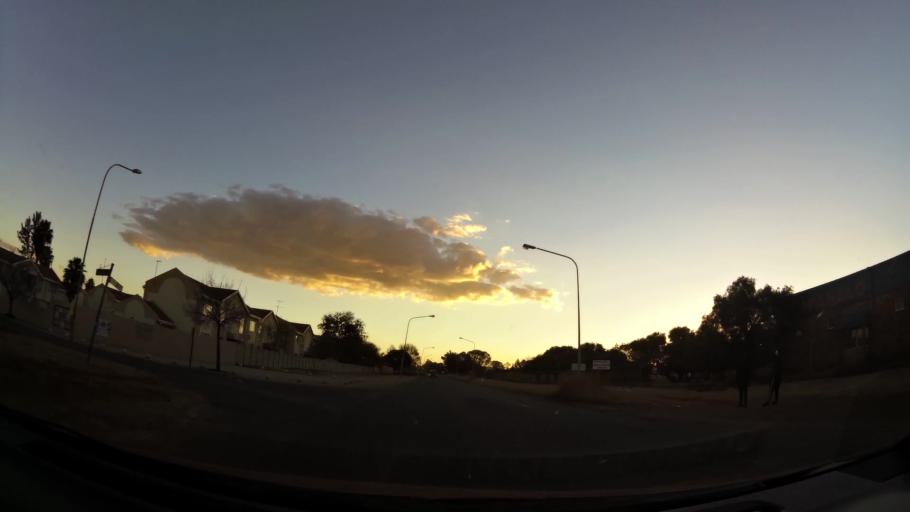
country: ZA
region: North-West
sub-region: Dr Kenneth Kaunda District Municipality
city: Potchefstroom
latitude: -26.6890
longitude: 27.0803
